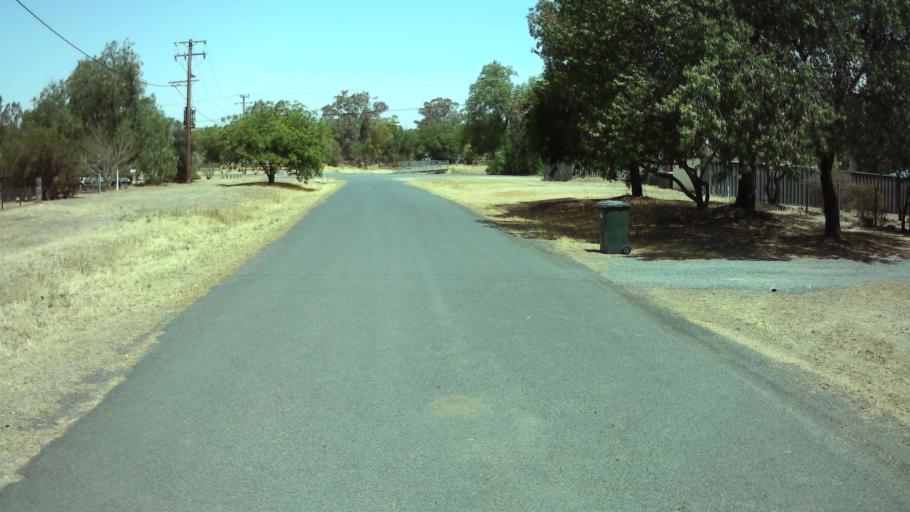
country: AU
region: New South Wales
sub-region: Weddin
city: Grenfell
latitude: -33.8888
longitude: 148.1540
